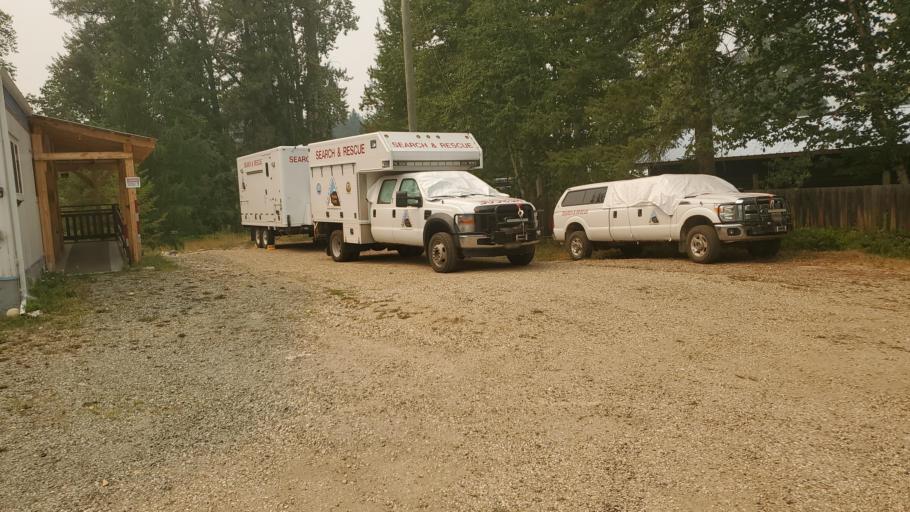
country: CA
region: British Columbia
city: Chase
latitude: 51.6476
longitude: -120.0639
